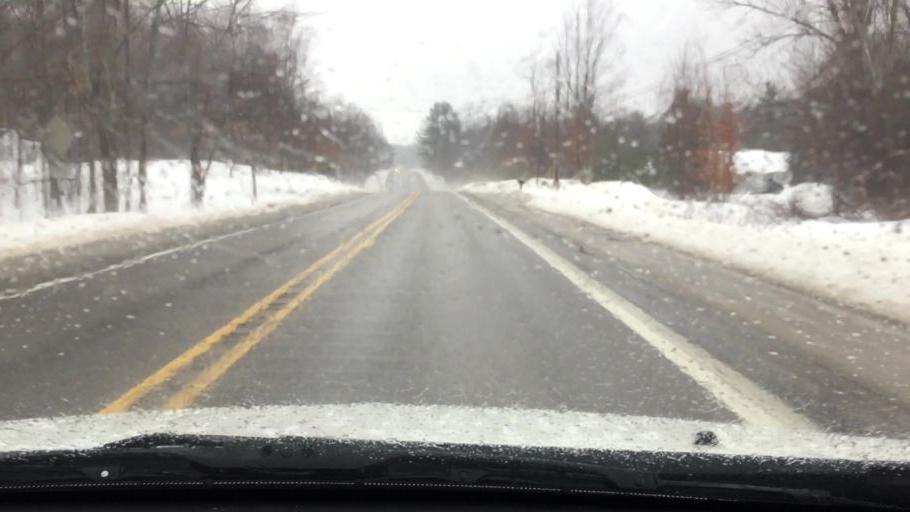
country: US
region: Michigan
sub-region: Charlevoix County
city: East Jordan
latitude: 45.2222
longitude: -85.1764
